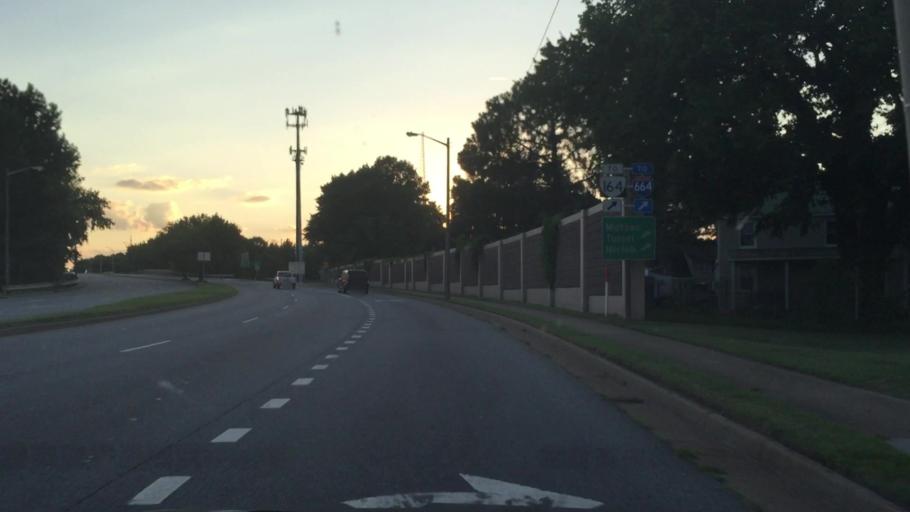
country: US
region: Virginia
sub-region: City of Portsmouth
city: Portsmouth
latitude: 36.8378
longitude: -76.3259
